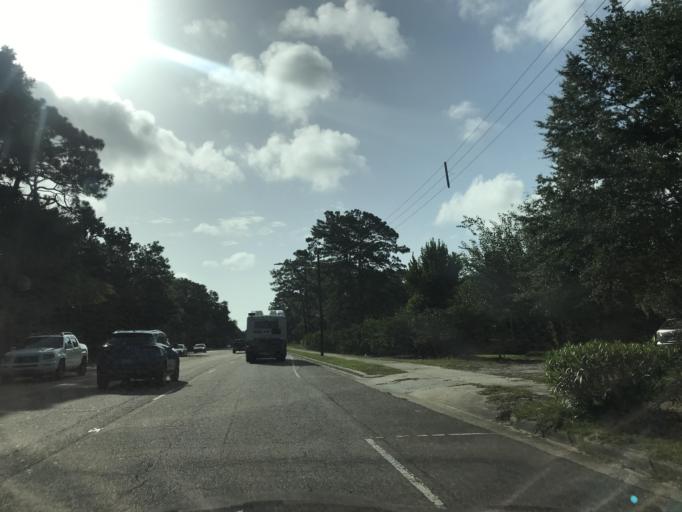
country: US
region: North Carolina
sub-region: New Hanover County
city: Wilmington
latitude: 34.2198
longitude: -77.9124
